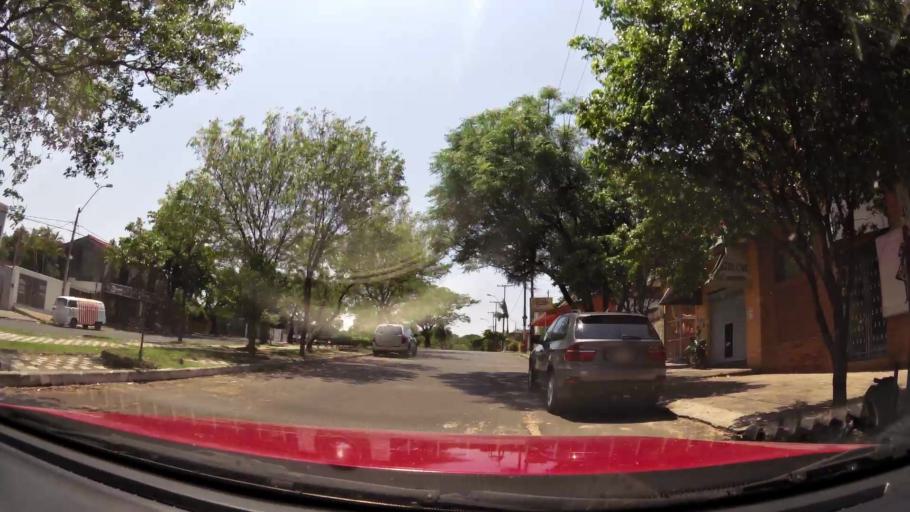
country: PY
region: Asuncion
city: Asuncion
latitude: -25.3014
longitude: -57.6360
